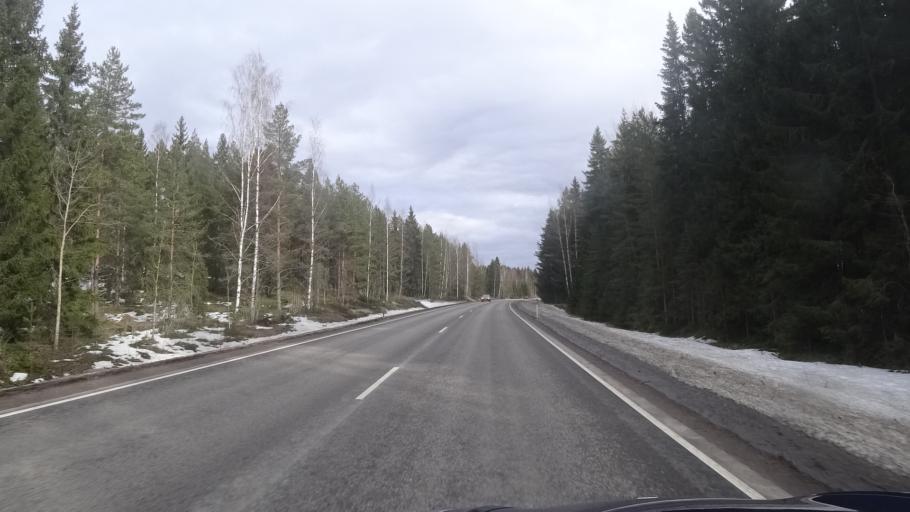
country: FI
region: Kymenlaakso
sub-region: Kouvola
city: Anjala
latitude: 60.6928
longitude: 26.7241
